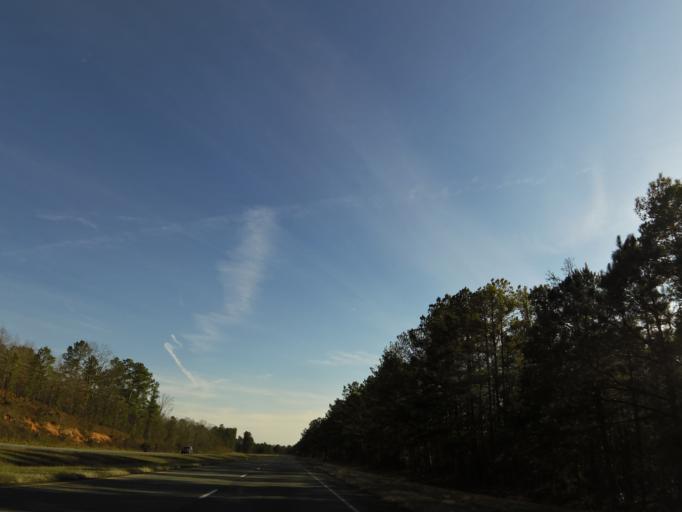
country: US
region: Georgia
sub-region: Stewart County
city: Richland
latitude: 32.1582
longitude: -84.6980
